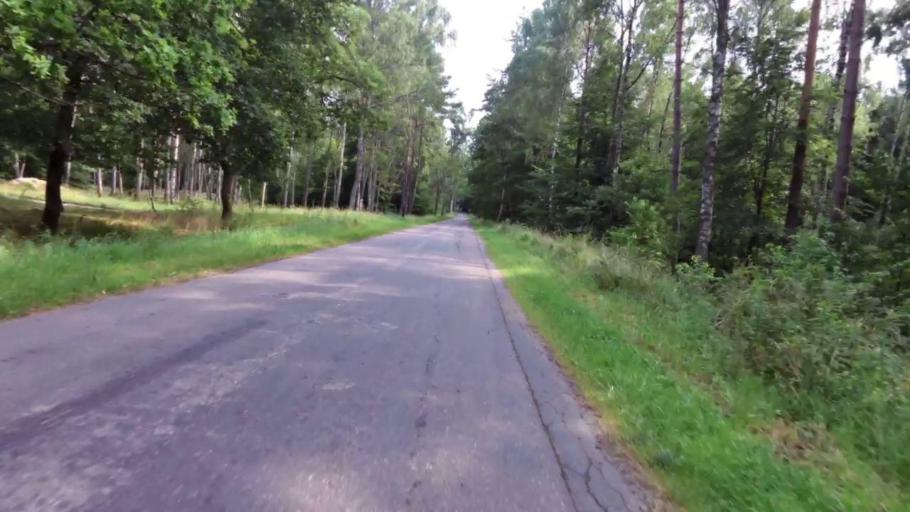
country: PL
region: West Pomeranian Voivodeship
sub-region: Powiat drawski
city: Zlocieniec
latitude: 53.5644
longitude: 15.9776
